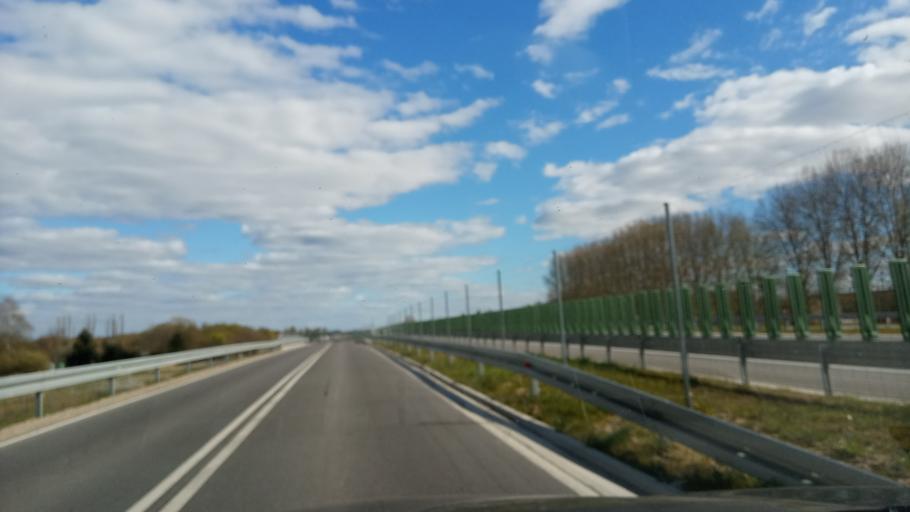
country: PL
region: West Pomeranian Voivodeship
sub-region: Powiat szczecinecki
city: Szczecinek
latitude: 53.7176
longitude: 16.7009
